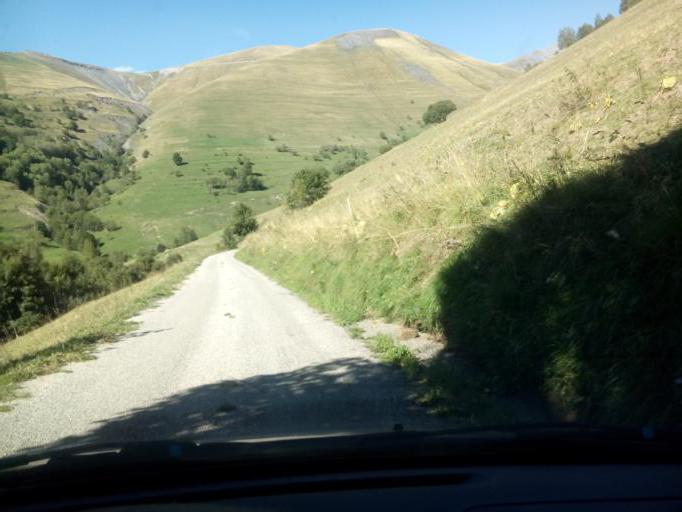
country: FR
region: Rhone-Alpes
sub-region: Departement de l'Isere
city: Mont-de-Lans
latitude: 45.0754
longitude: 6.1806
